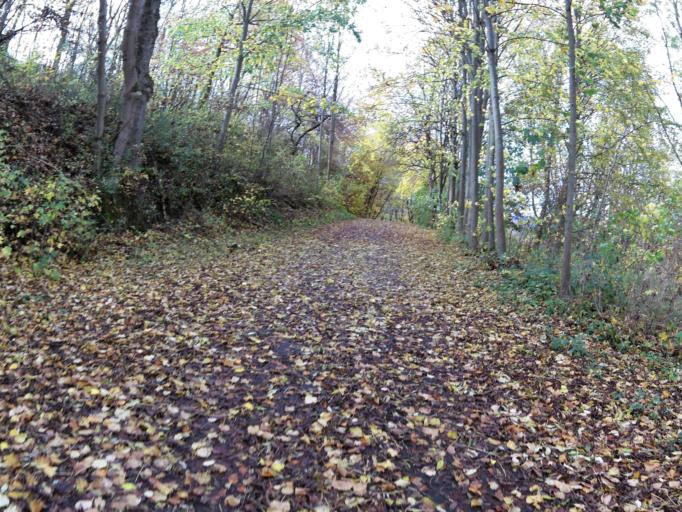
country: DE
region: Thuringia
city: Ifta
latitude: 51.0696
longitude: 10.1345
